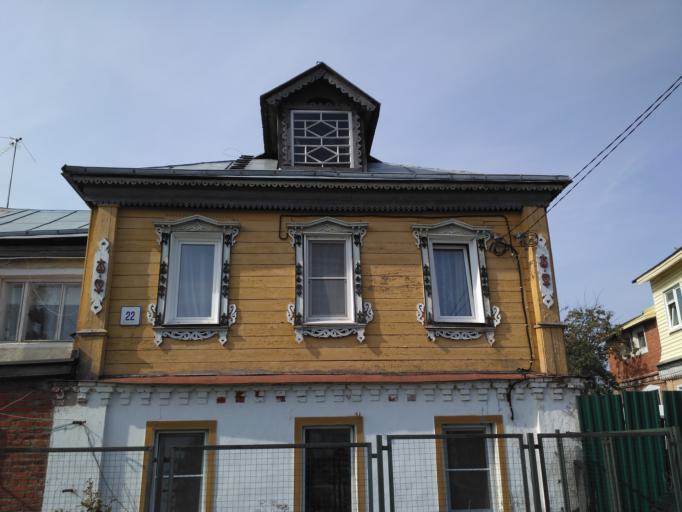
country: RU
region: Moskovskaya
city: Sergiyev Posad
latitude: 56.3104
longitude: 38.1247
